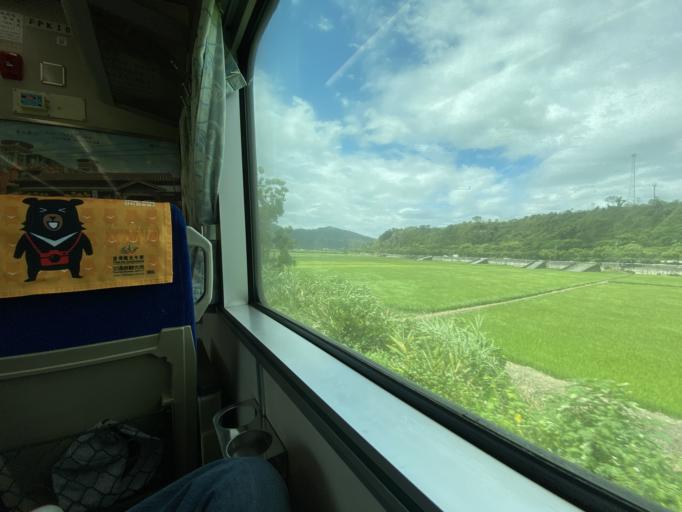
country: TW
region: Taiwan
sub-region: Taitung
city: Taitung
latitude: 22.8995
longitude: 121.1382
